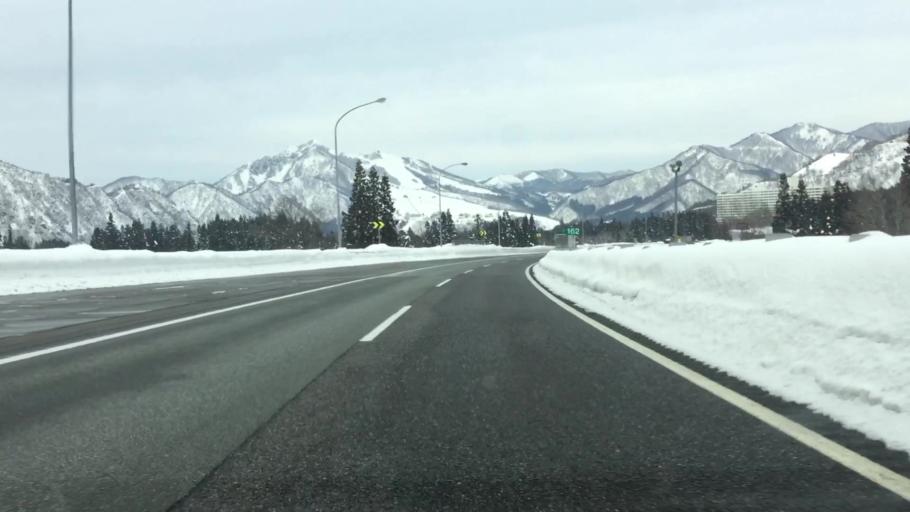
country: JP
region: Niigata
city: Shiozawa
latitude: 36.8957
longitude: 138.8452
